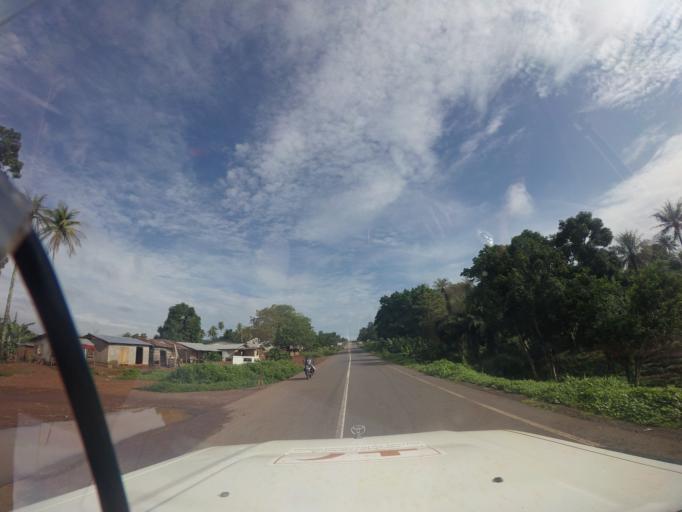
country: SL
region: Northern Province
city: Kambia
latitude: 9.1207
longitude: -12.9326
